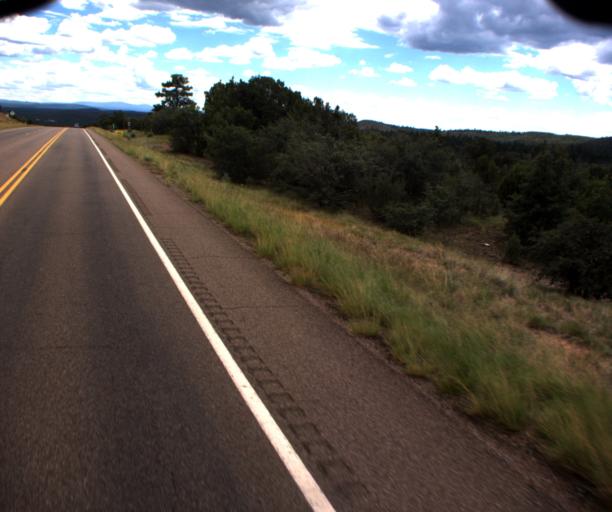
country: US
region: Arizona
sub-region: Navajo County
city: Linden
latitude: 34.2958
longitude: -110.1882
